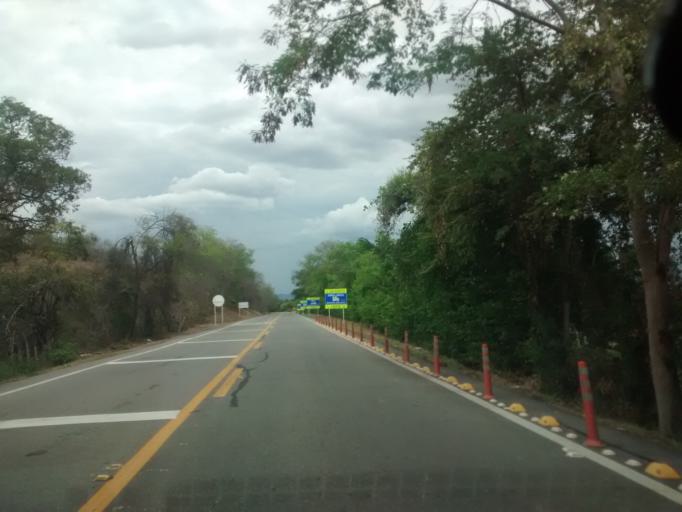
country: CO
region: Cundinamarca
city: Agua de Dios
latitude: 4.4040
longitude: -74.7247
